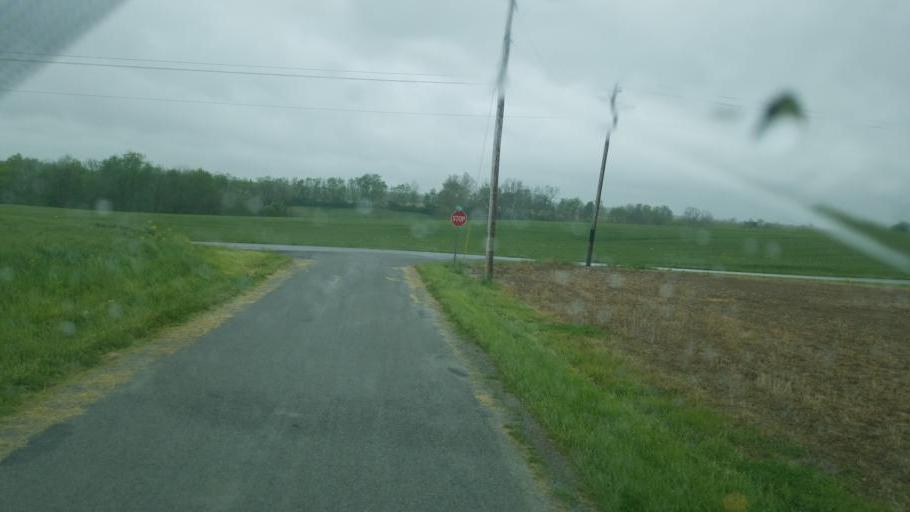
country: US
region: Ohio
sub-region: Highland County
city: Greenfield
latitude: 39.3345
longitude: -83.4579
